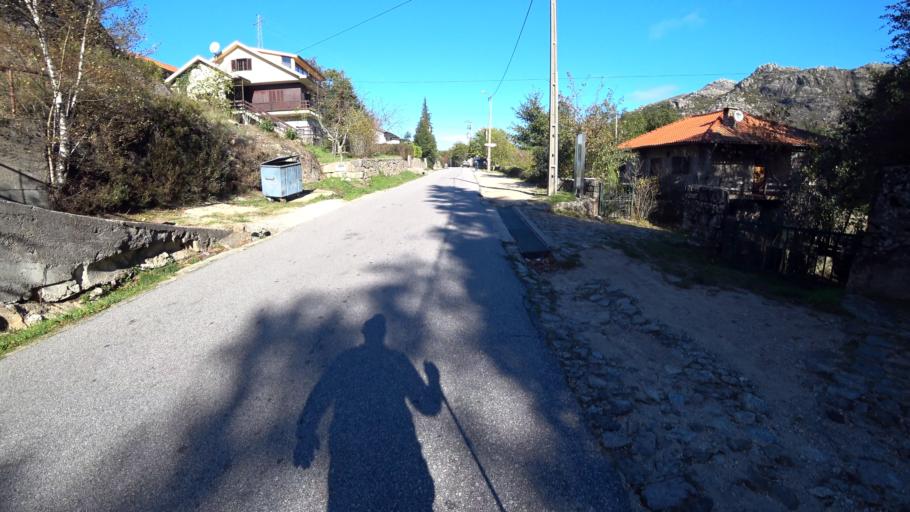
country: PT
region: Braga
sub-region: Terras de Bouro
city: Antas
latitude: 41.7591
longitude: -8.1932
